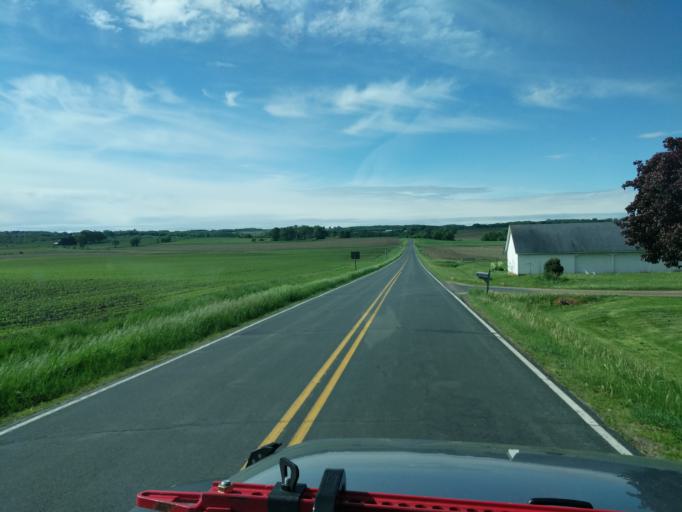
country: US
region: Wisconsin
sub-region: Saint Croix County
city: Hammond
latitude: 44.9129
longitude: -92.4863
